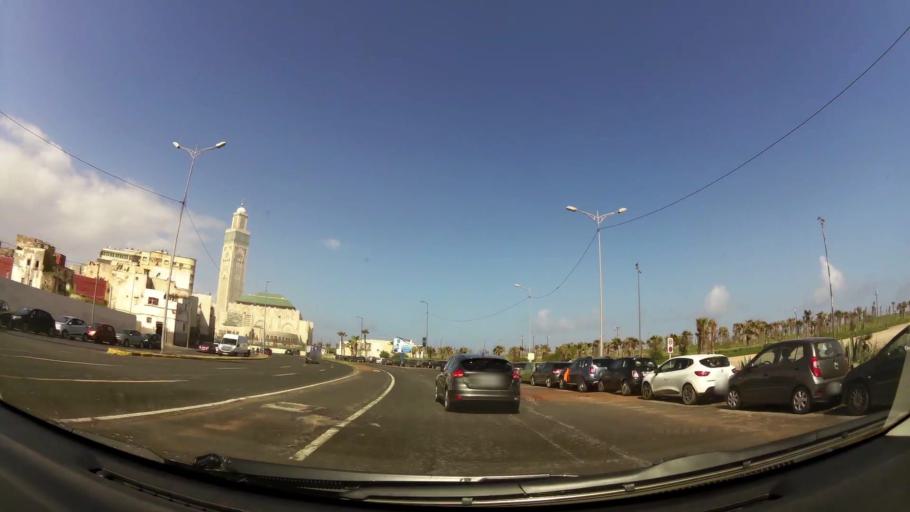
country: MA
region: Grand Casablanca
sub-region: Casablanca
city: Casablanca
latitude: 33.6087
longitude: -7.6261
